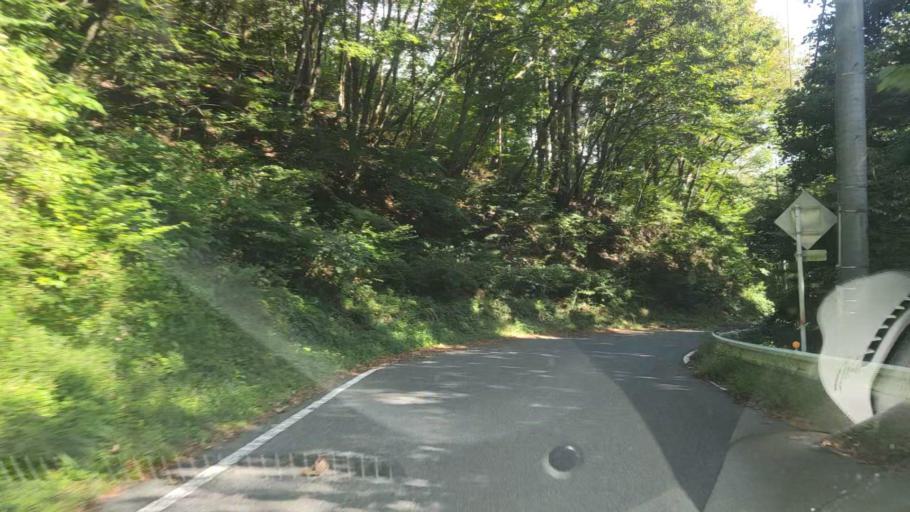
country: JP
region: Gunma
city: Nakanojomachi
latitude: 36.5957
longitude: 138.6861
